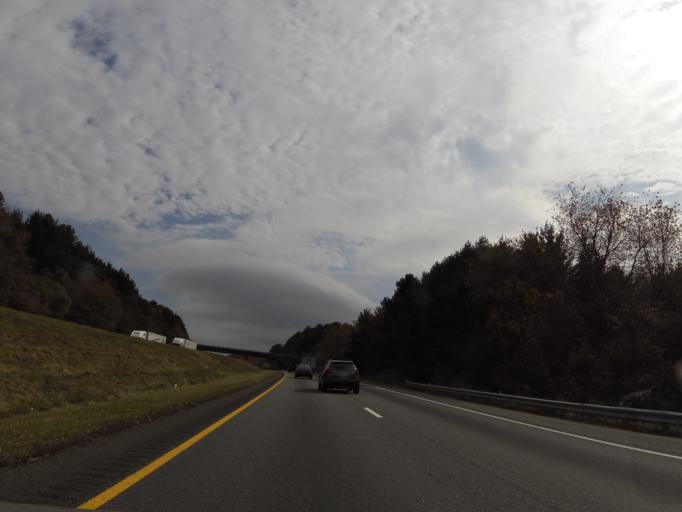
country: US
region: Virginia
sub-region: Carroll County
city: Hillsville
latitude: 36.6974
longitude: -80.7374
